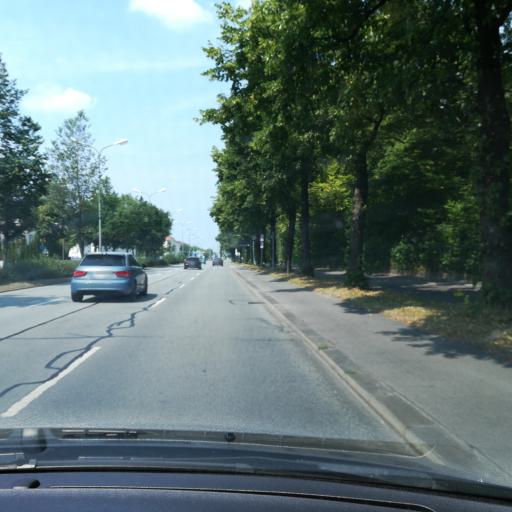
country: DE
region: Bavaria
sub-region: Upper Bavaria
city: Neuried
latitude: 48.1229
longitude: 11.5028
